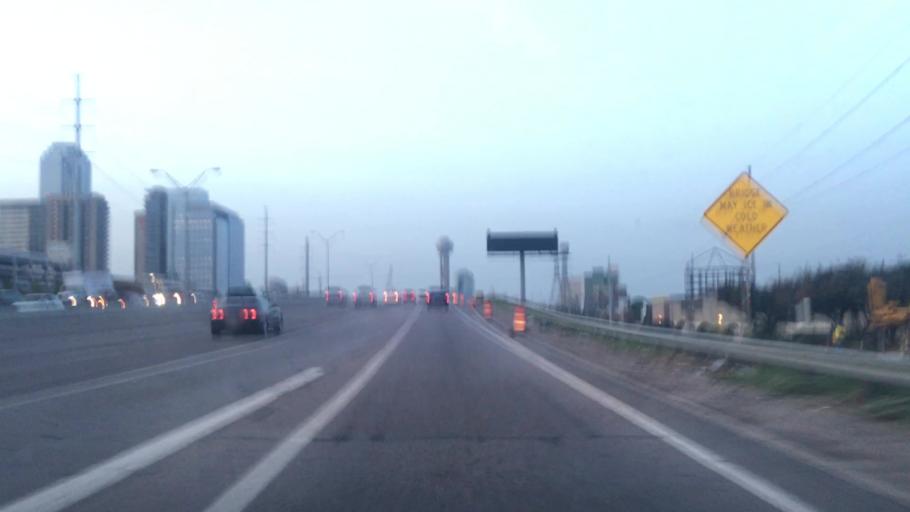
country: US
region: Texas
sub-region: Dallas County
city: Dallas
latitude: 32.7905
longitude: -96.8140
